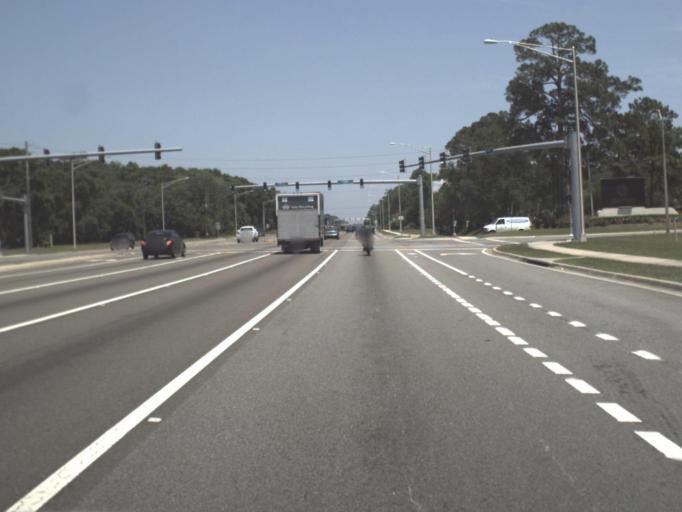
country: US
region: Florida
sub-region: Duval County
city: Neptune Beach
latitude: 30.2870
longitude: -81.5114
